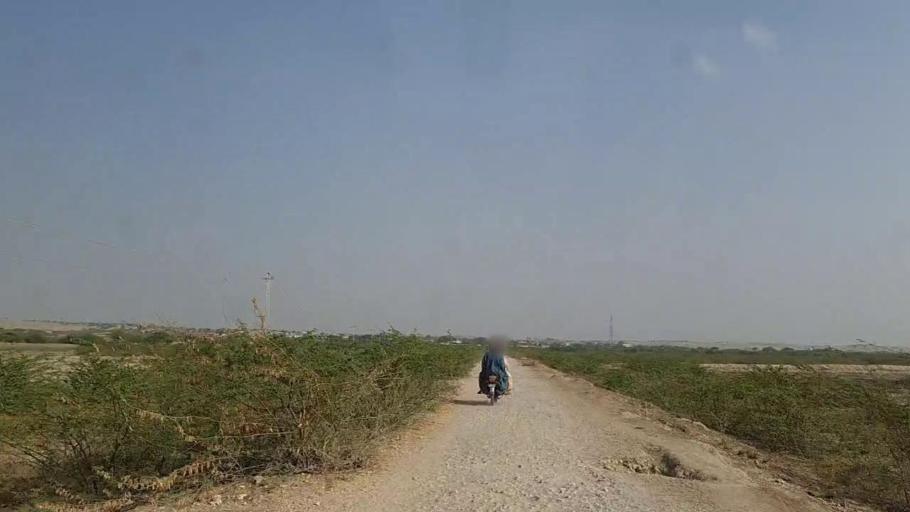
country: PK
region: Sindh
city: Naukot
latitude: 24.6634
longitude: 69.2823
